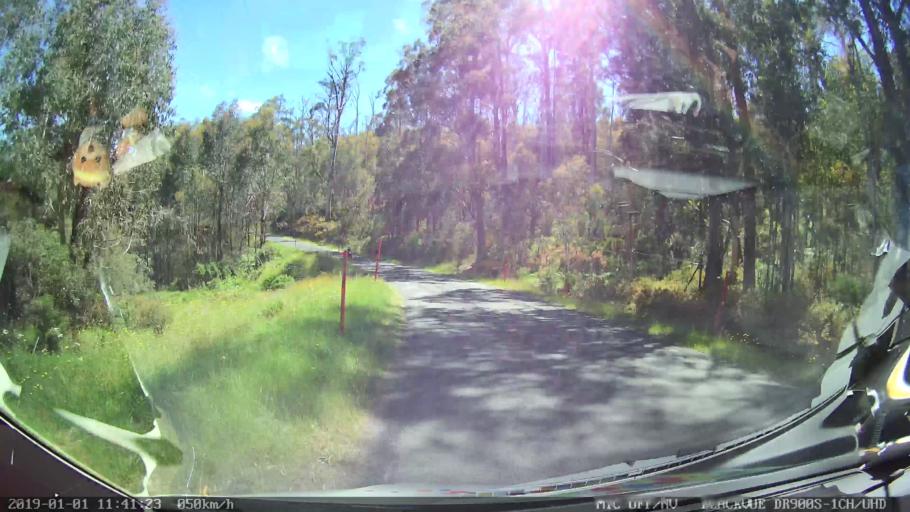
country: AU
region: New South Wales
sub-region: Snowy River
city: Jindabyne
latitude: -35.9144
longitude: 148.3905
